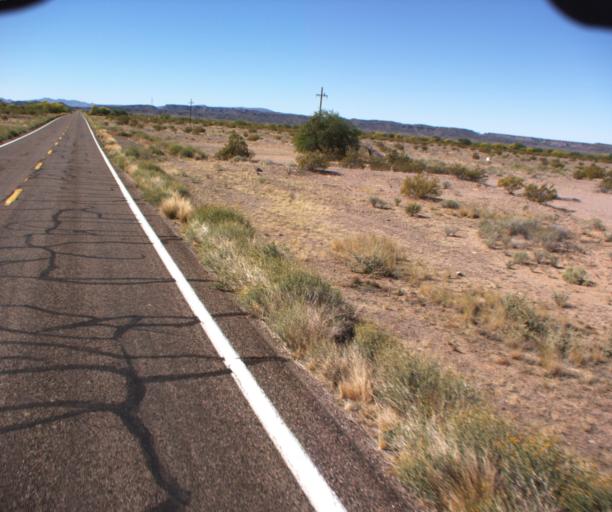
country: US
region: Arizona
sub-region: Pima County
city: Ajo
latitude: 32.6202
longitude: -112.8668
